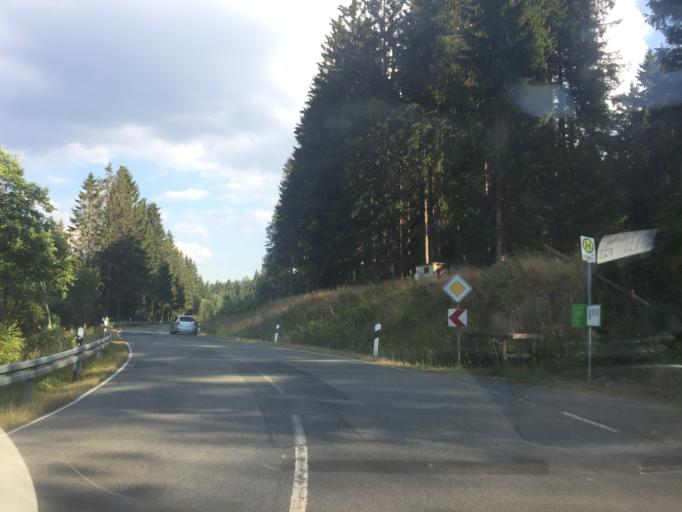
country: DE
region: Lower Saxony
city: Braunlage
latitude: 51.6995
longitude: 10.6222
